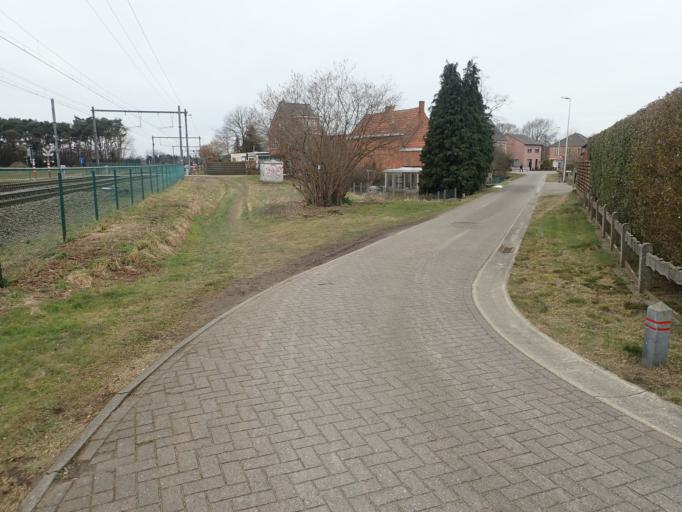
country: BE
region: Flanders
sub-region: Provincie Antwerpen
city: Nijlen
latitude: 51.1618
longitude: 4.6938
